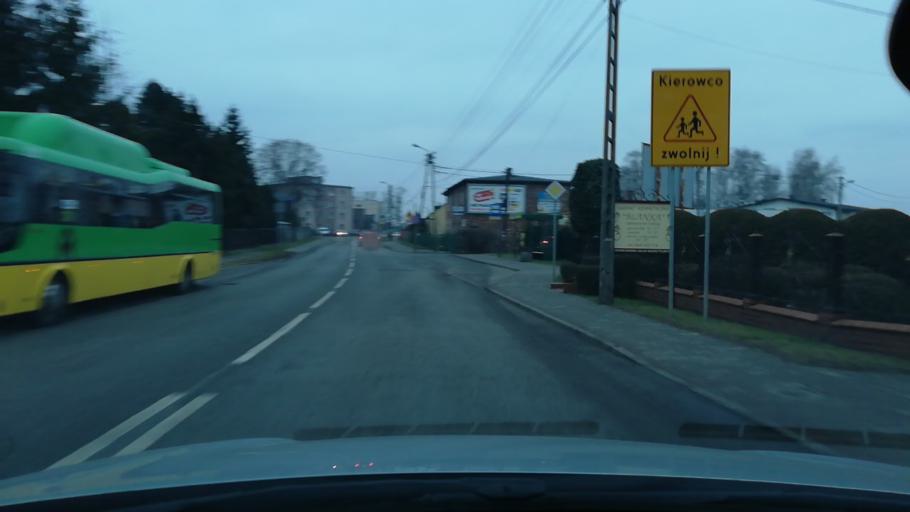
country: PL
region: Silesian Voivodeship
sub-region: Ruda Slaska
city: Ruda Slaska
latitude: 50.2467
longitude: 18.8365
